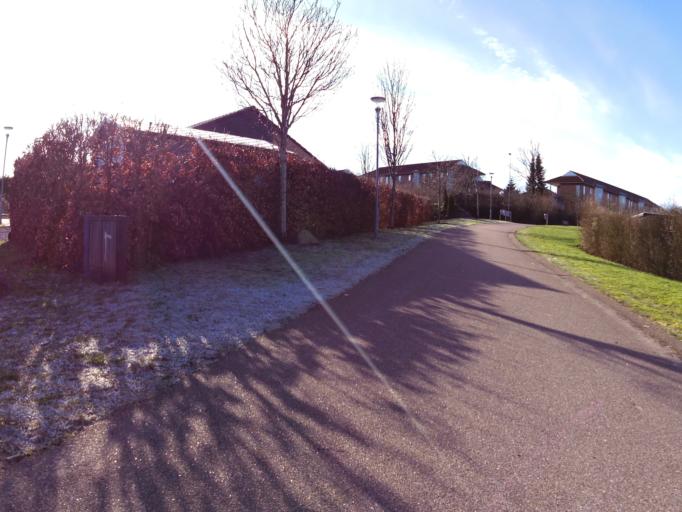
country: DK
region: Central Jutland
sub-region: Arhus Kommune
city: Kolt
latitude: 56.1117
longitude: 10.0834
